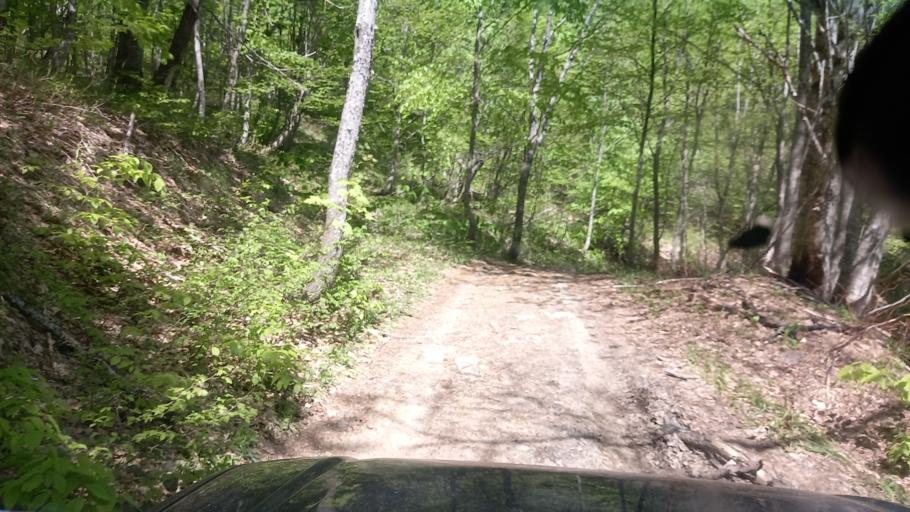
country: RU
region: Krasnodarskiy
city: Tuapse
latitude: 44.2465
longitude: 39.2931
